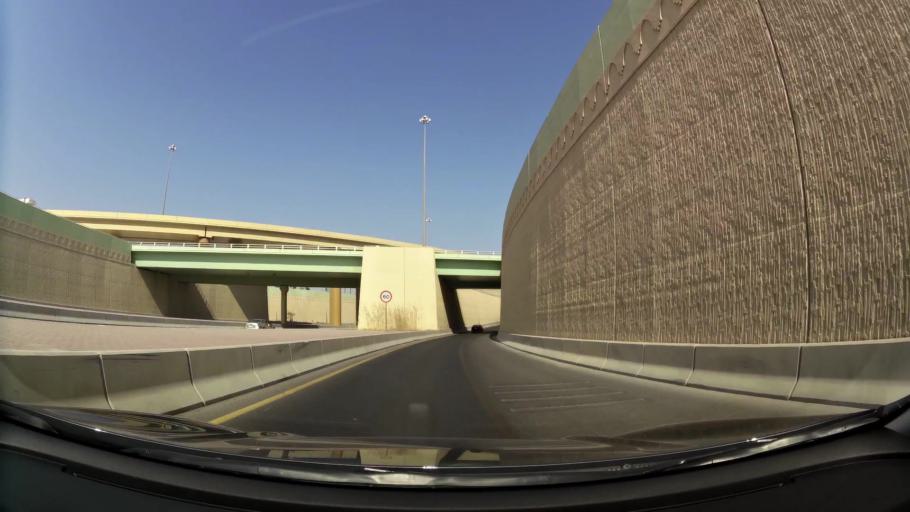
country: KW
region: Al Asimah
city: Ash Shamiyah
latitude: 29.3610
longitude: 47.9611
